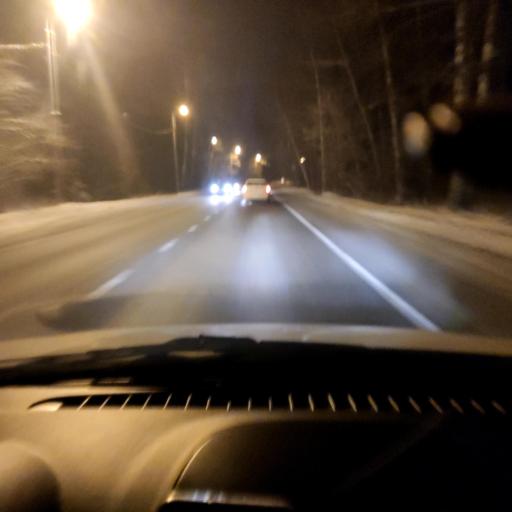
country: RU
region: Tatarstan
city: Osinovo
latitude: 55.8343
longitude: 48.8930
